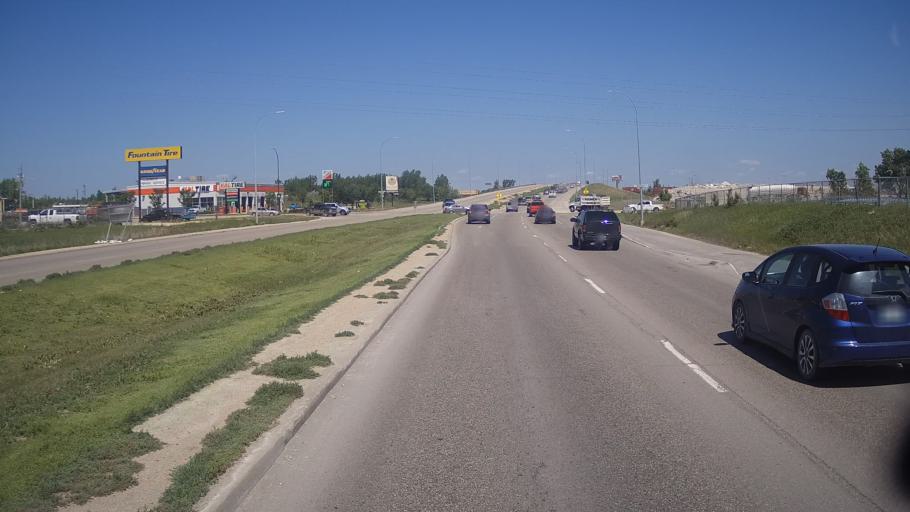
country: CA
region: Manitoba
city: Winnipeg
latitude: 49.8898
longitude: -97.0721
